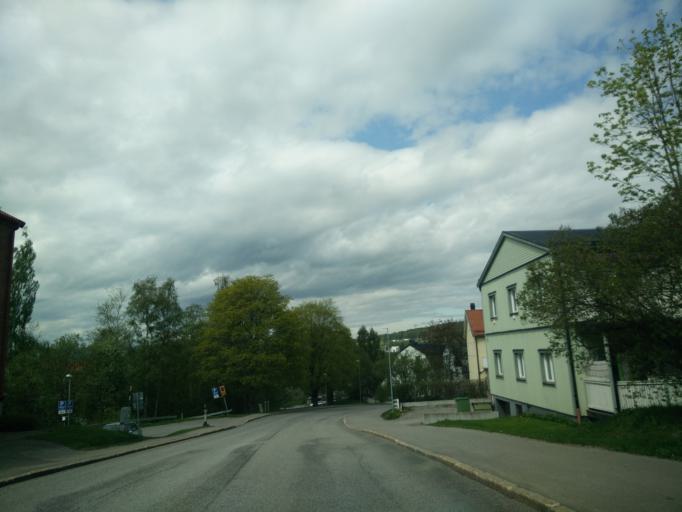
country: SE
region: Vaesternorrland
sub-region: Sundsvalls Kommun
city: Sundsvall
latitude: 62.3859
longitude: 17.2828
